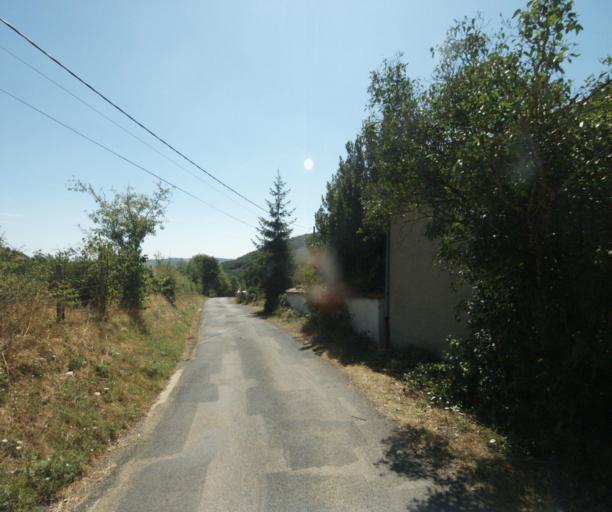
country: FR
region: Rhone-Alpes
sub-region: Departement du Rhone
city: Bessenay
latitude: 45.7928
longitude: 4.5240
